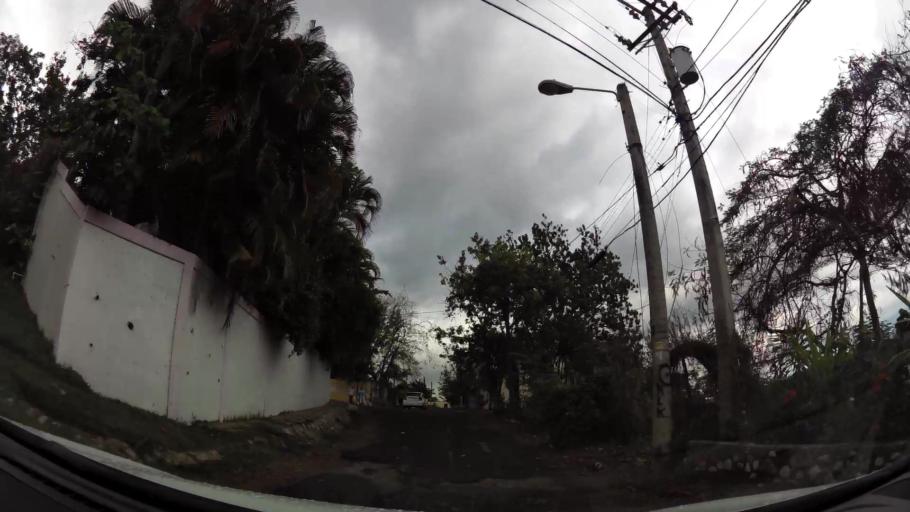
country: DO
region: Nacional
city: La Agustina
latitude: 18.5053
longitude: -69.9345
